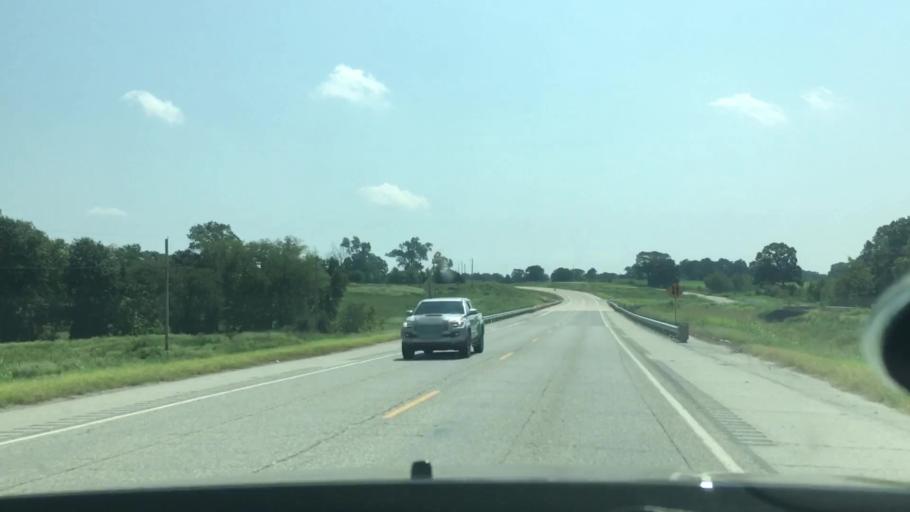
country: US
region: Oklahoma
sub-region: Atoka County
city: Atoka
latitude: 34.2920
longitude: -95.9739
